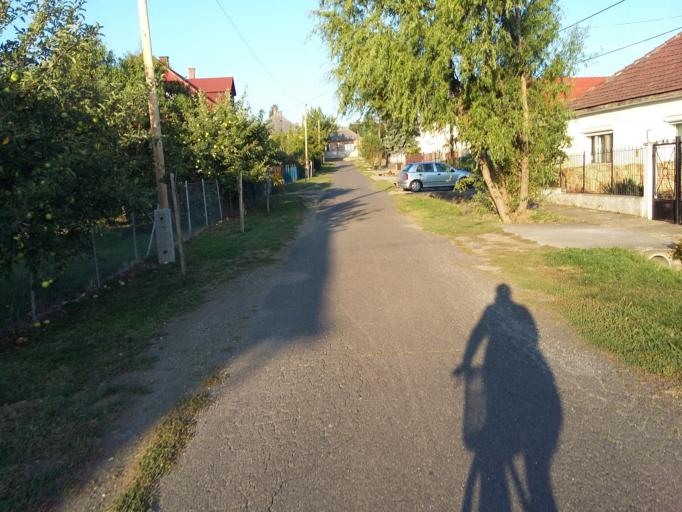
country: HU
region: Borsod-Abauj-Zemplen
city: Bekecs
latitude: 48.1616
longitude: 21.1804
